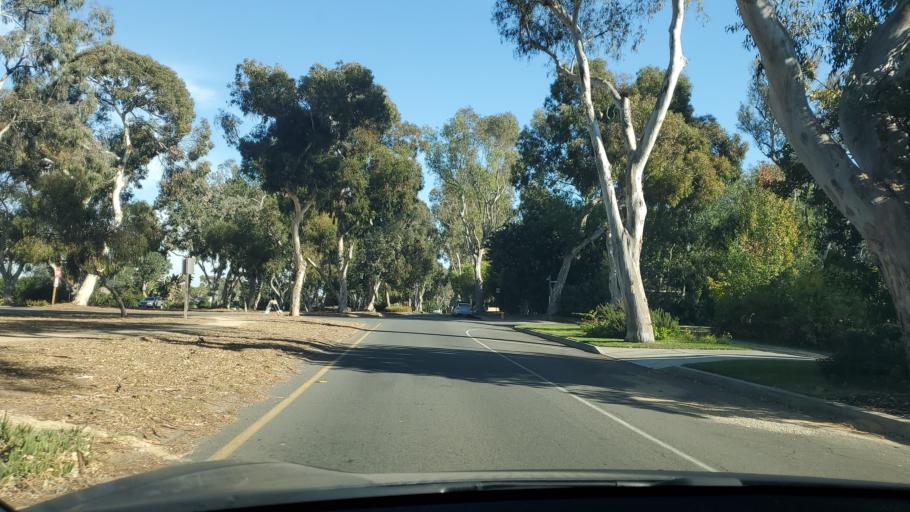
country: US
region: California
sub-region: Los Angeles County
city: Palos Verdes Estates
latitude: 33.8026
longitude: -118.3749
